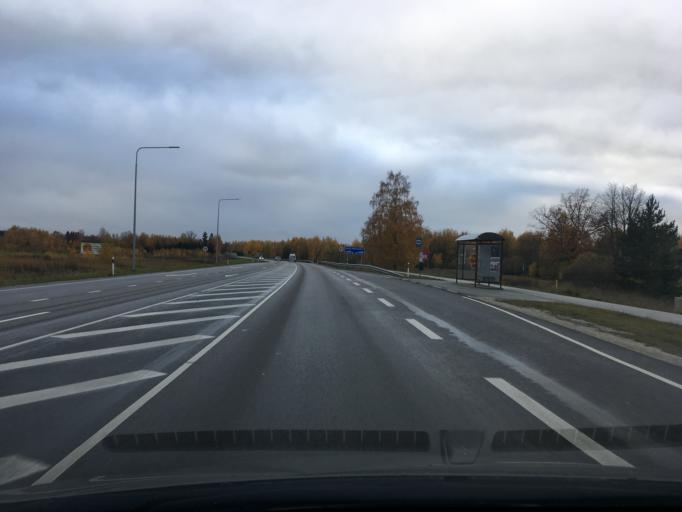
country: EE
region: Tartu
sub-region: UElenurme vald
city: Ulenurme
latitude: 58.3398
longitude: 26.6542
